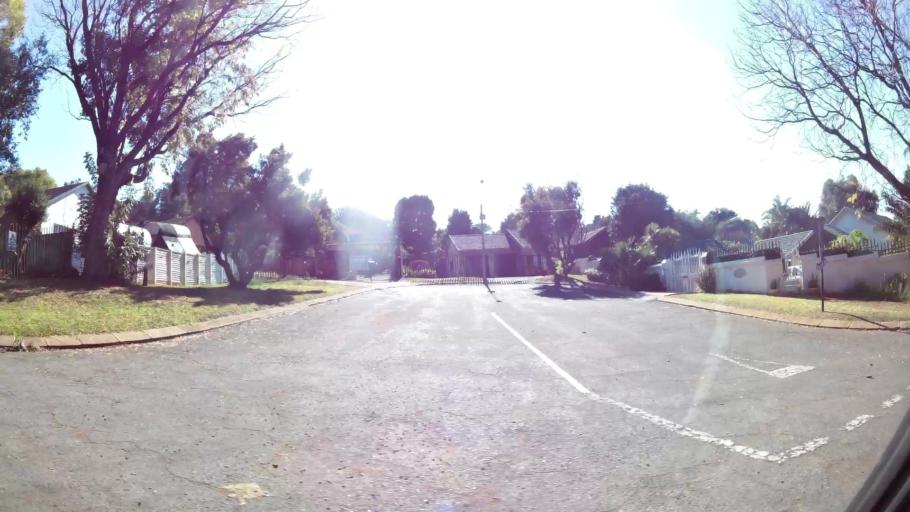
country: ZA
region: Gauteng
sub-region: City of Johannesburg Metropolitan Municipality
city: Roodepoort
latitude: -26.1198
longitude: 27.8635
